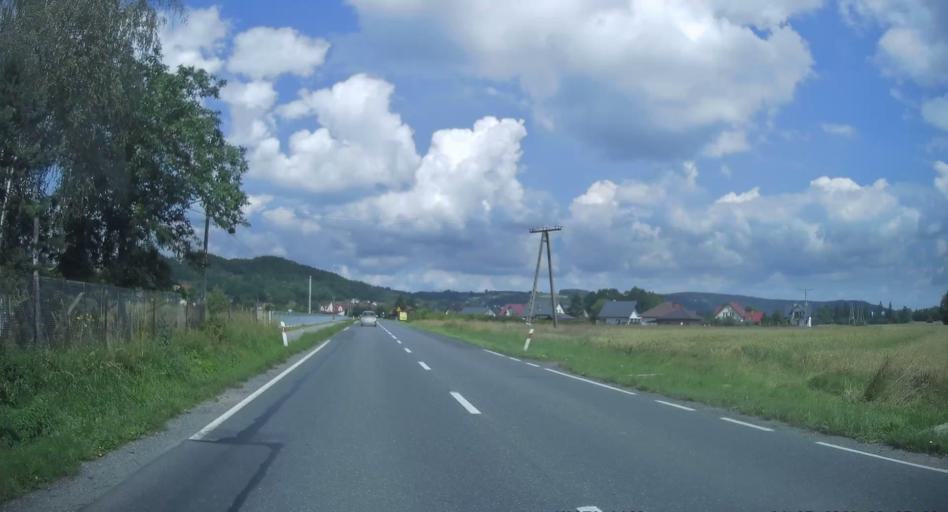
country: PL
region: Lesser Poland Voivodeship
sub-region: Powiat tarnowski
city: Zakliczyn
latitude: 49.8898
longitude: 20.8238
